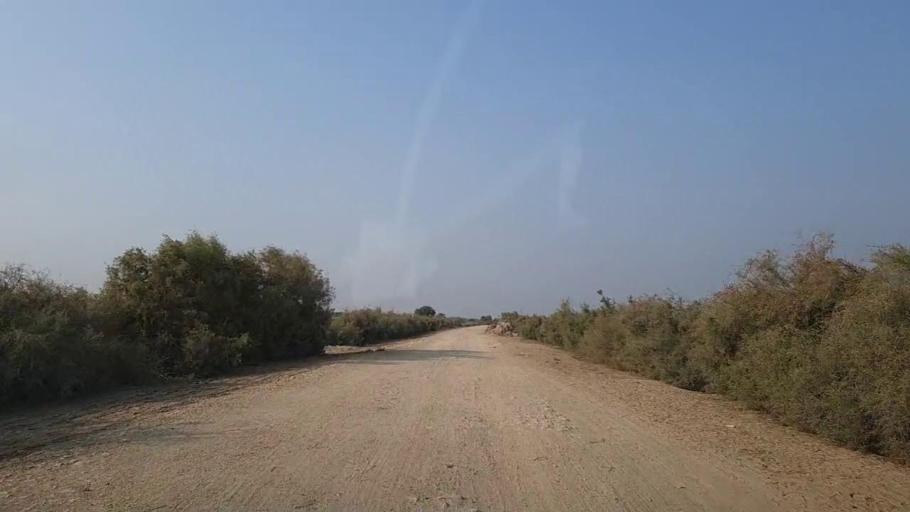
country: PK
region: Sindh
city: Mirpur Sakro
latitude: 24.6341
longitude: 67.7674
